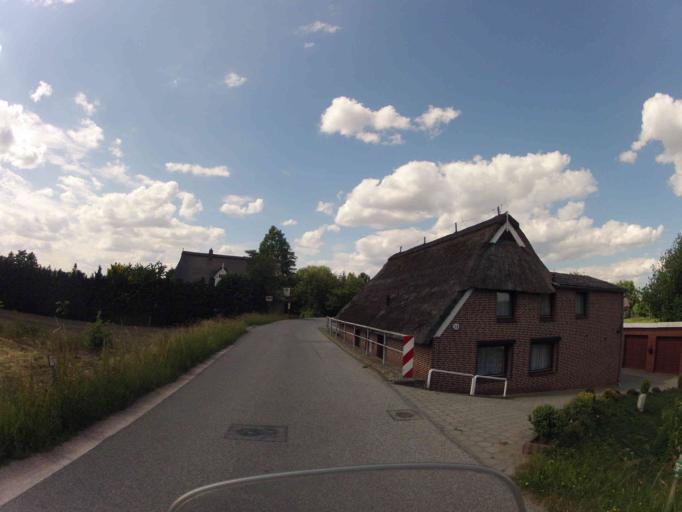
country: DE
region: Hamburg
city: Rothenburgsort
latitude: 53.4780
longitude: 10.0994
